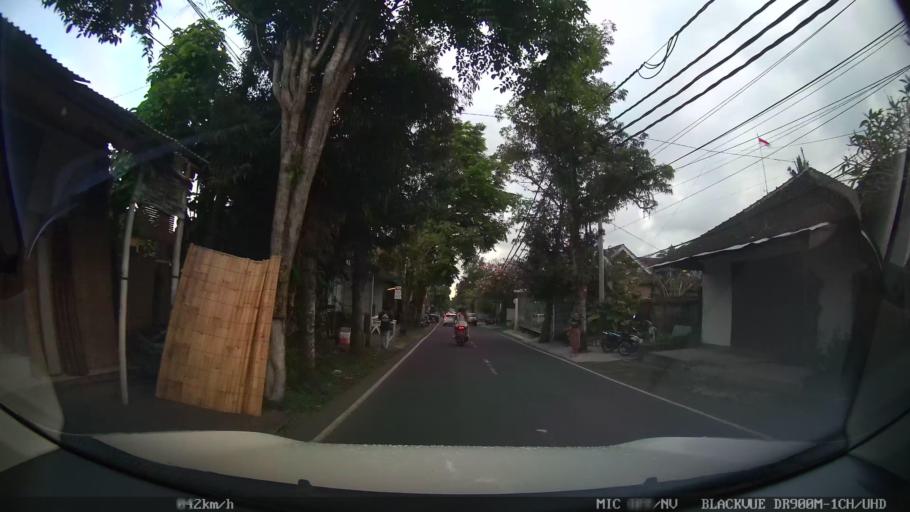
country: ID
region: Bali
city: Banjar Pande
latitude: -8.5018
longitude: 115.2441
